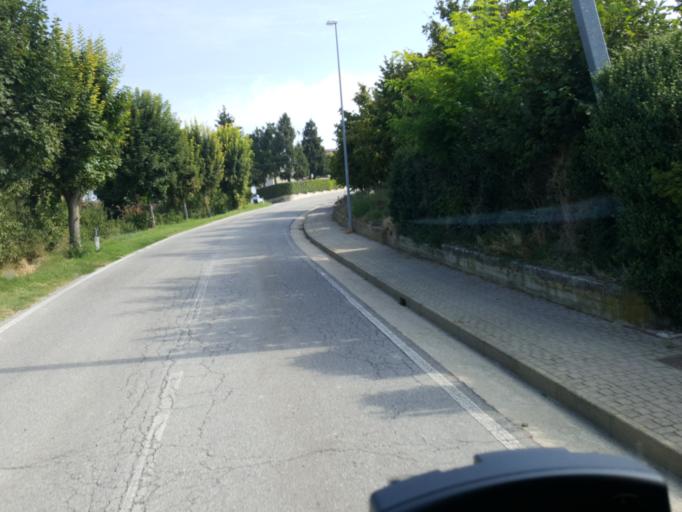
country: IT
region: Piedmont
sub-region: Provincia di Cuneo
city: Novello
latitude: 44.5918
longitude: 7.9261
